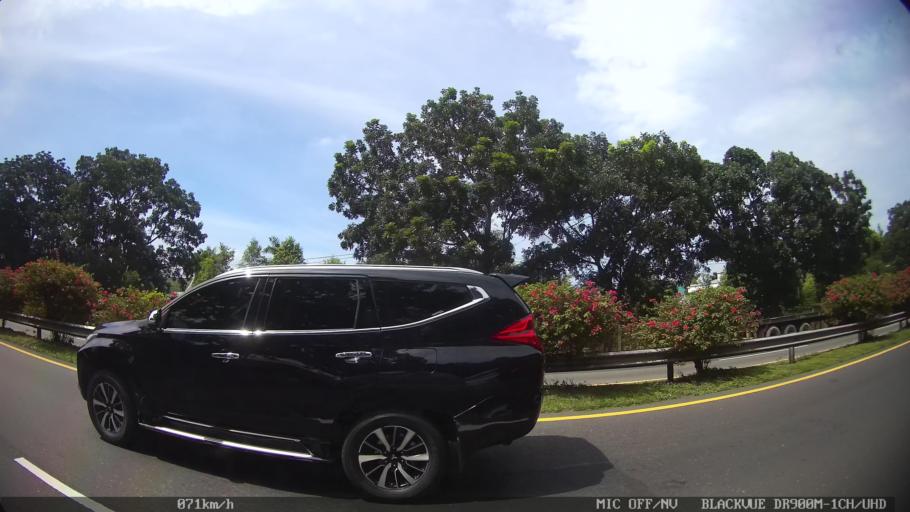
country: ID
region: North Sumatra
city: Medan
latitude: 3.6414
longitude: 98.6969
